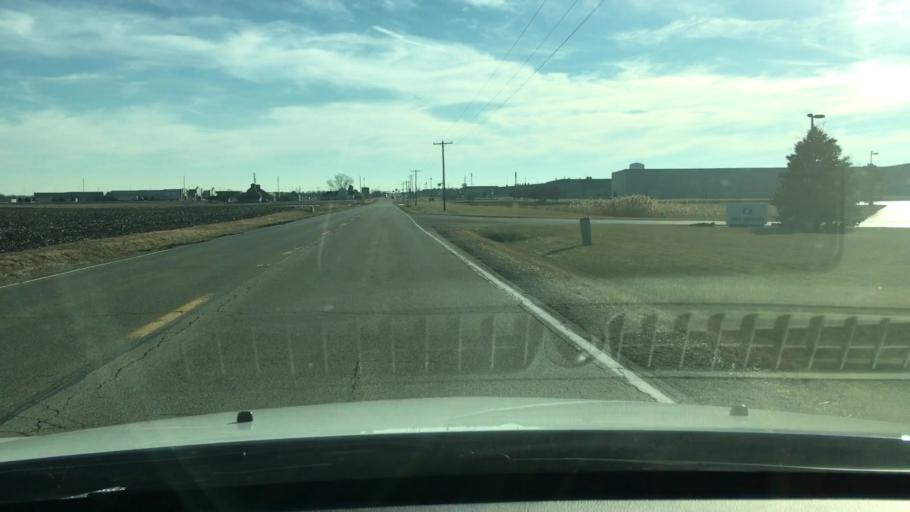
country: US
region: Illinois
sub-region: LaSalle County
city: Peru
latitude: 41.3811
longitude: -89.1257
